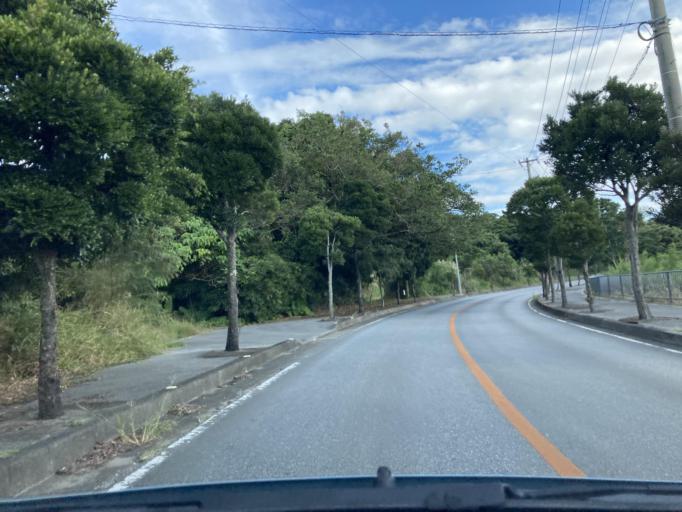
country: JP
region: Okinawa
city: Itoman
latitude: 26.1345
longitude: 127.7221
